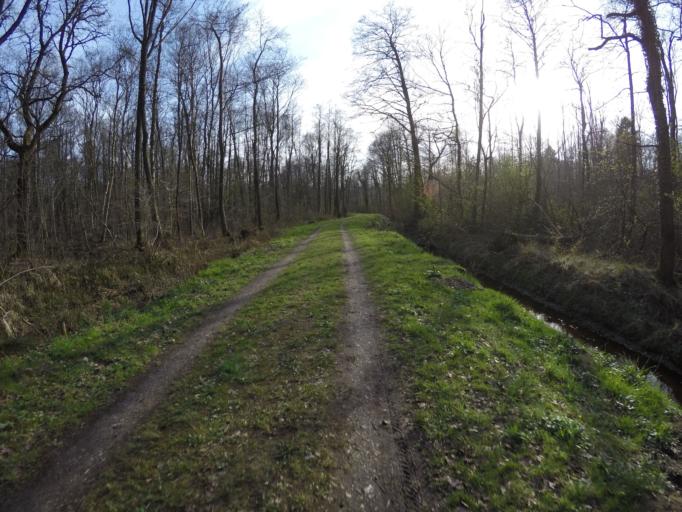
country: DE
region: Schleswig-Holstein
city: Hemdingen
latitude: 53.7431
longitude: 9.8335
